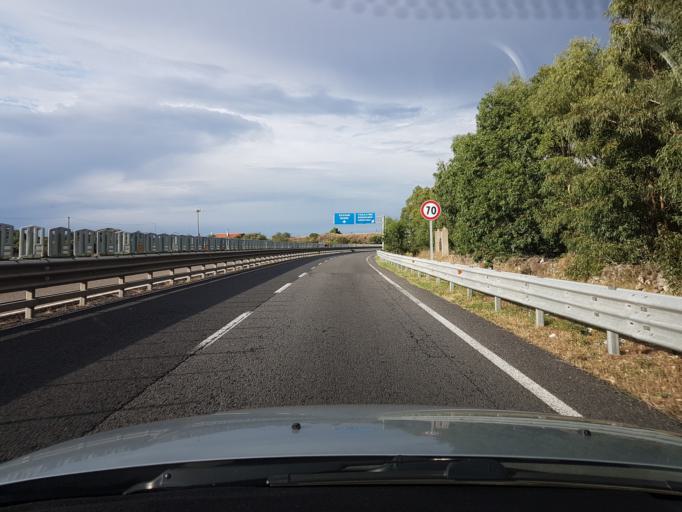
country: IT
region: Sardinia
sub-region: Provincia di Oristano
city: Paulilatino
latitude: 40.0884
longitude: 8.7553
